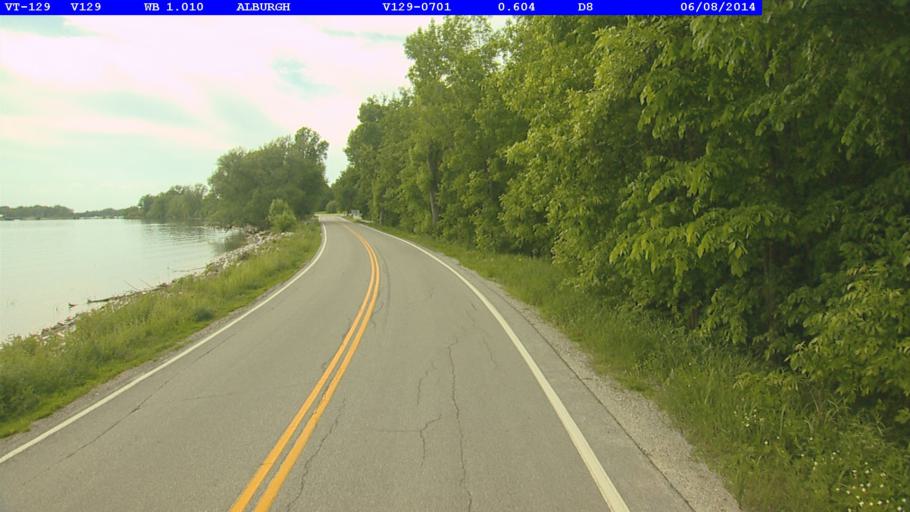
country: US
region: Vermont
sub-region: Grand Isle County
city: North Hero
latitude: 44.9028
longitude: -73.3044
